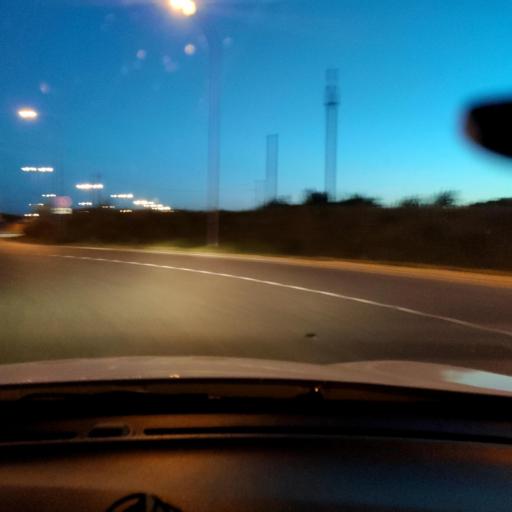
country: RU
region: Tatarstan
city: Osinovo
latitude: 55.8582
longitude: 48.8397
